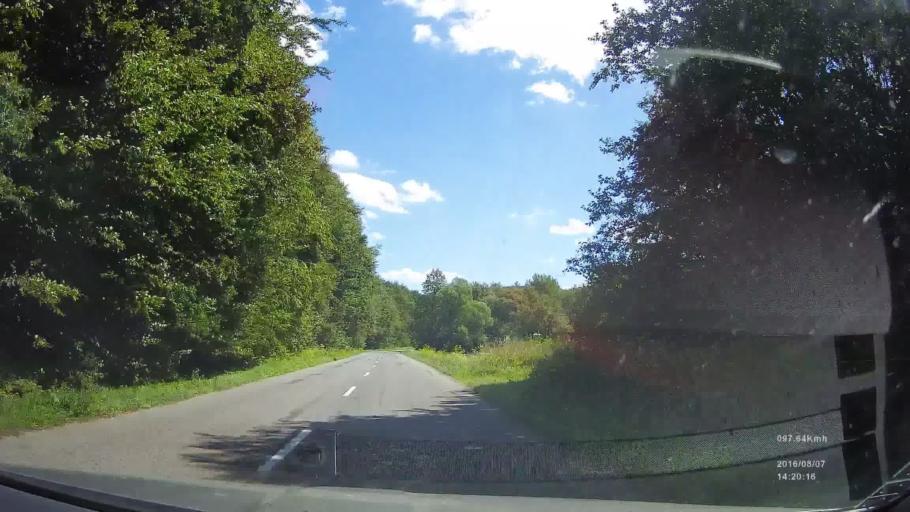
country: SK
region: Presovsky
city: Stropkov
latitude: 49.2923
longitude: 21.7605
